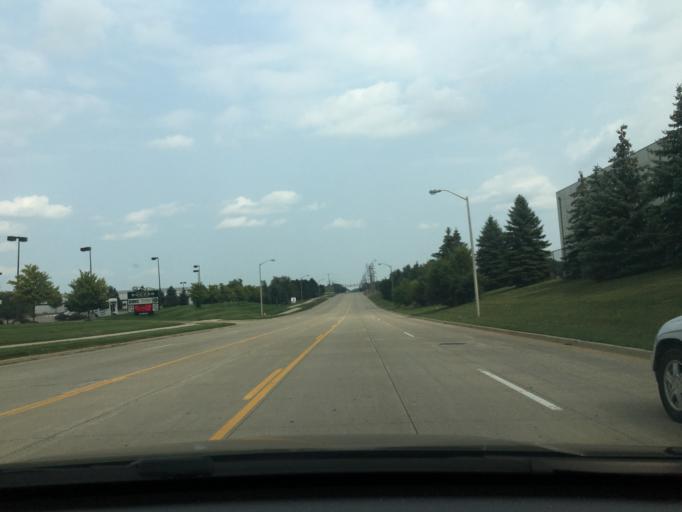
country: US
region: Michigan
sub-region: Oakland County
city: Bloomfield Hills
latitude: 42.6198
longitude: -83.2550
